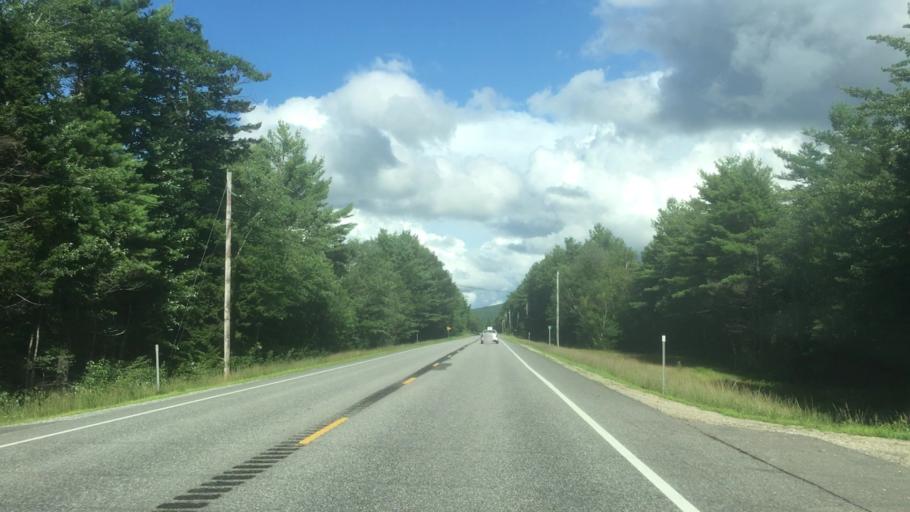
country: US
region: New Hampshire
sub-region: Cheshire County
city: Harrisville
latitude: 43.0372
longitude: -72.0958
